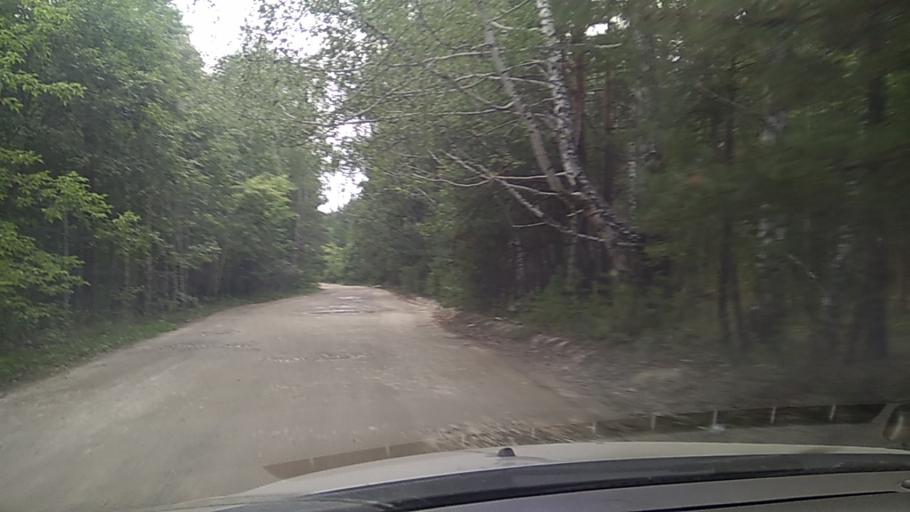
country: RU
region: Chelyabinsk
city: Kyshtym
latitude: 55.6786
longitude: 60.5831
